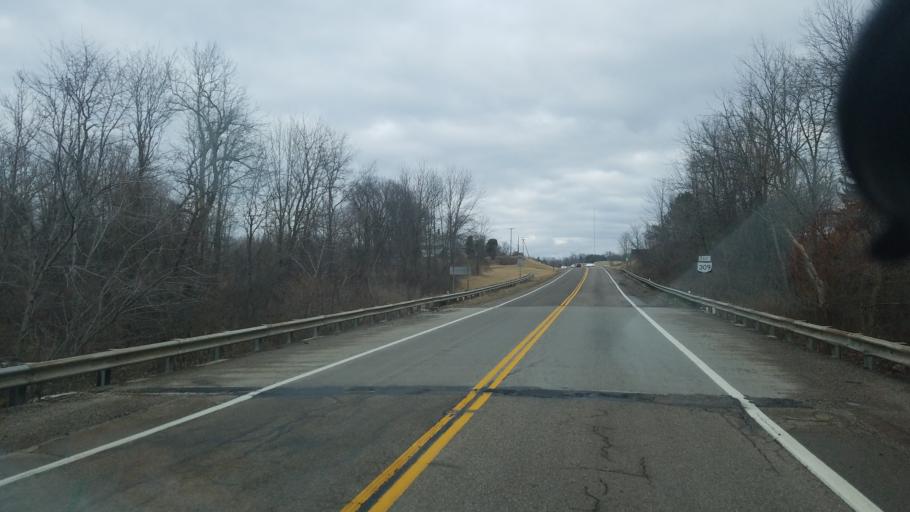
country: US
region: Ohio
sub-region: Crawford County
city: Galion
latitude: 40.6657
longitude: -82.8588
